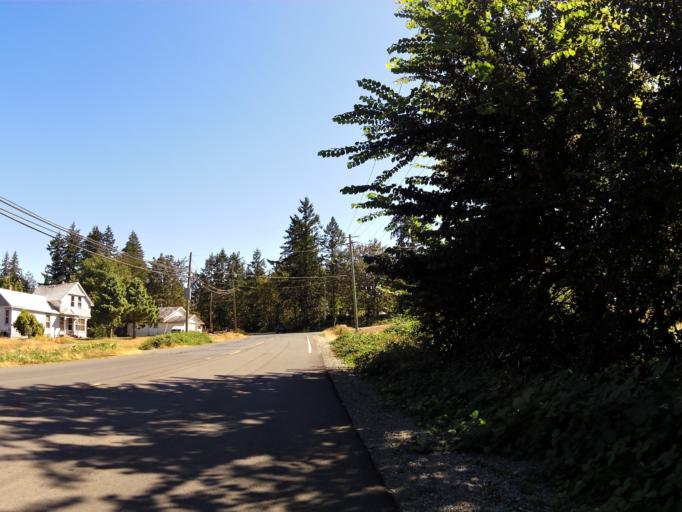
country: CA
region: British Columbia
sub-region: Cowichan Valley Regional District
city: Ladysmith
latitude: 48.9455
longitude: -123.7595
